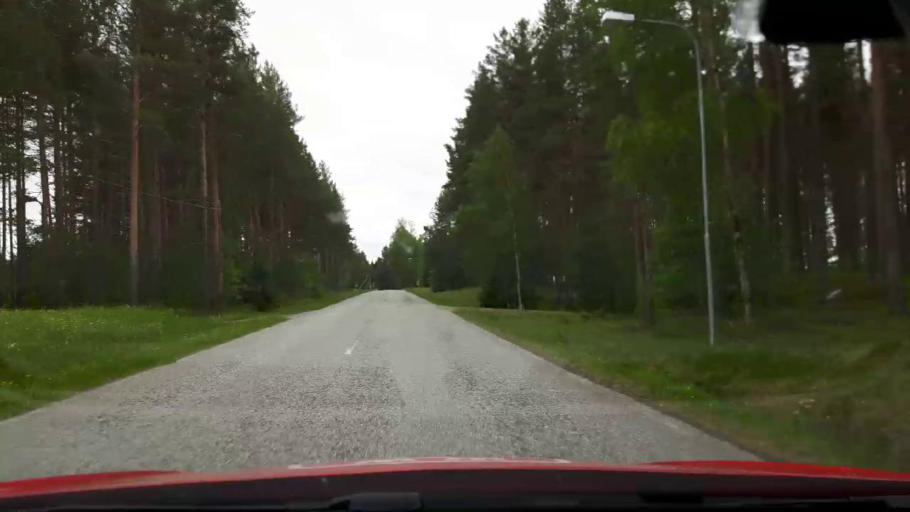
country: SE
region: Jaemtland
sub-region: Ragunda Kommun
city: Hammarstrand
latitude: 63.2213
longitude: 15.9352
